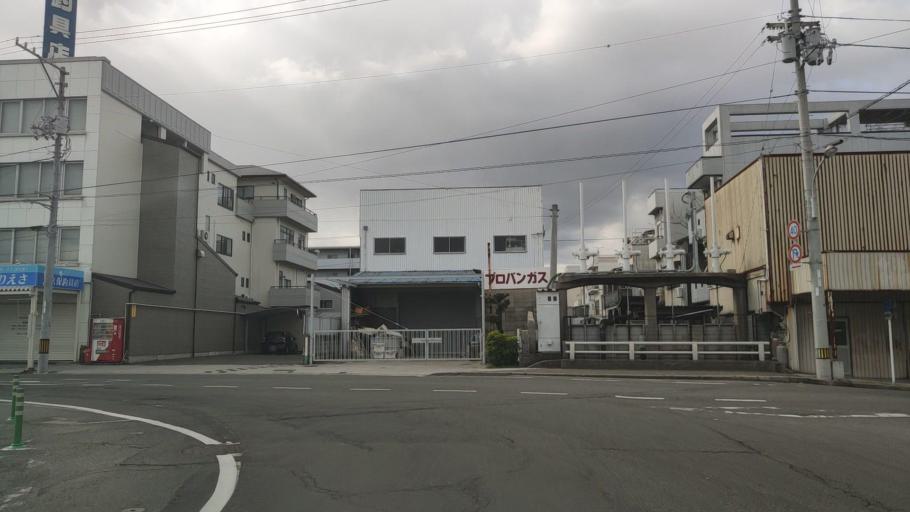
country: JP
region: Ehime
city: Saijo
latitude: 34.0686
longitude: 133.0048
